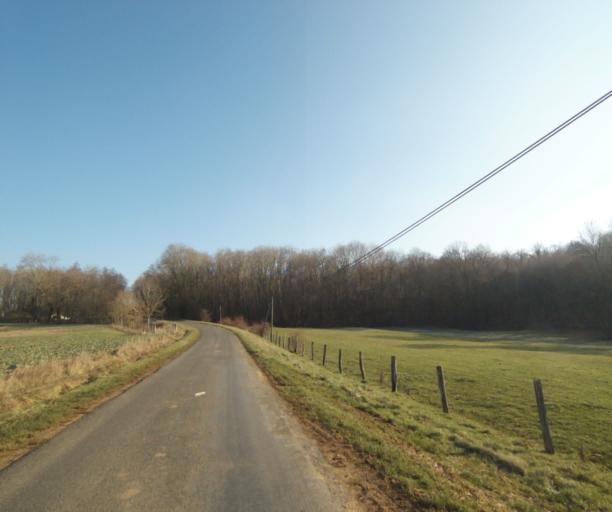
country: FR
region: Champagne-Ardenne
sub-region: Departement de la Haute-Marne
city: Bienville
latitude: 48.5080
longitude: 5.0266
